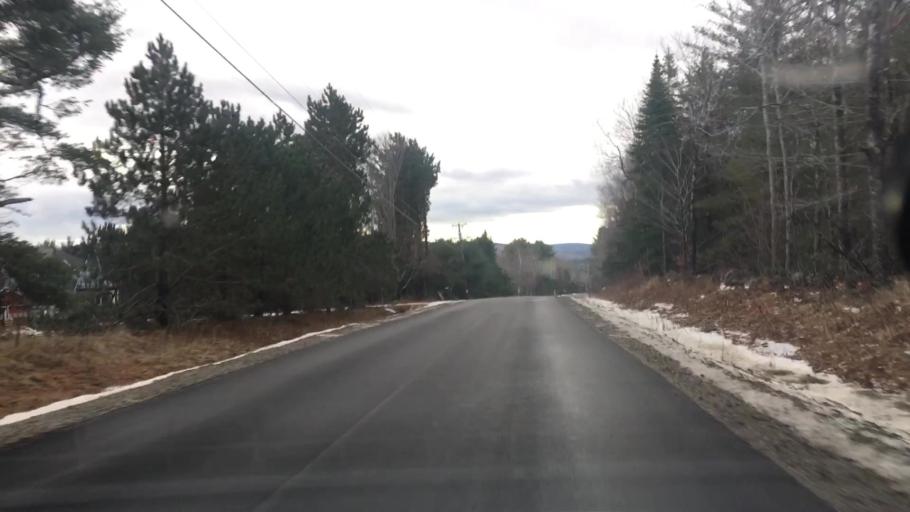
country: US
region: Maine
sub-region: Hancock County
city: Dedham
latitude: 44.6580
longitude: -68.7046
